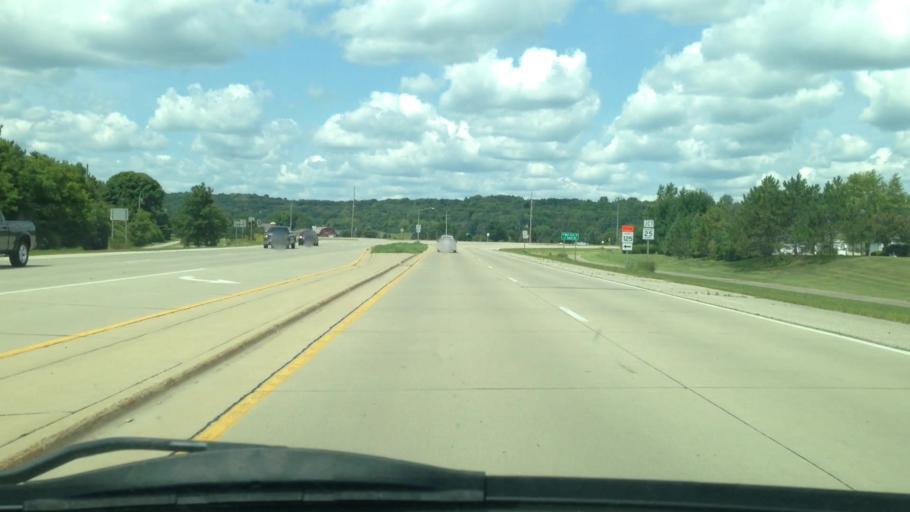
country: US
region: Minnesota
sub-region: Olmsted County
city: Rochester
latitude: 44.0028
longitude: -92.5046
